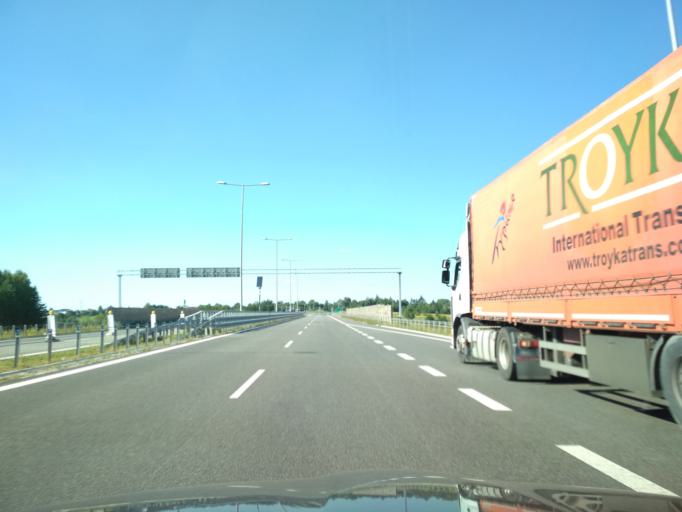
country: PL
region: Subcarpathian Voivodeship
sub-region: Powiat rzeszowski
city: Kielanowka
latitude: 50.0190
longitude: 21.9218
